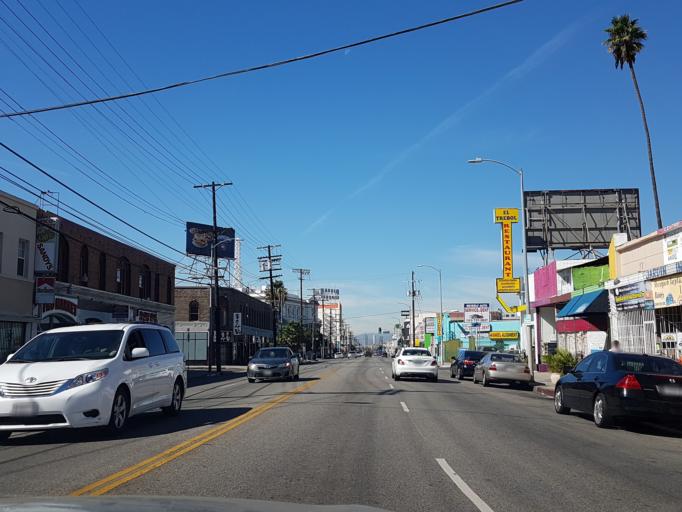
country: US
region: California
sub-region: Los Angeles County
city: Hollywood
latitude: 34.0474
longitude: -118.3218
